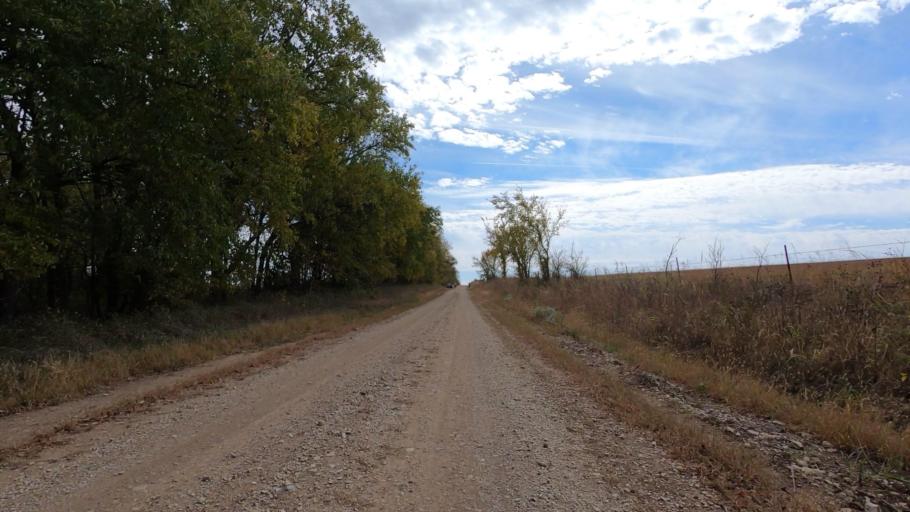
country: US
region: Kansas
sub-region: Pottawatomie County
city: Westmoreland
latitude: 39.3332
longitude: -96.4453
